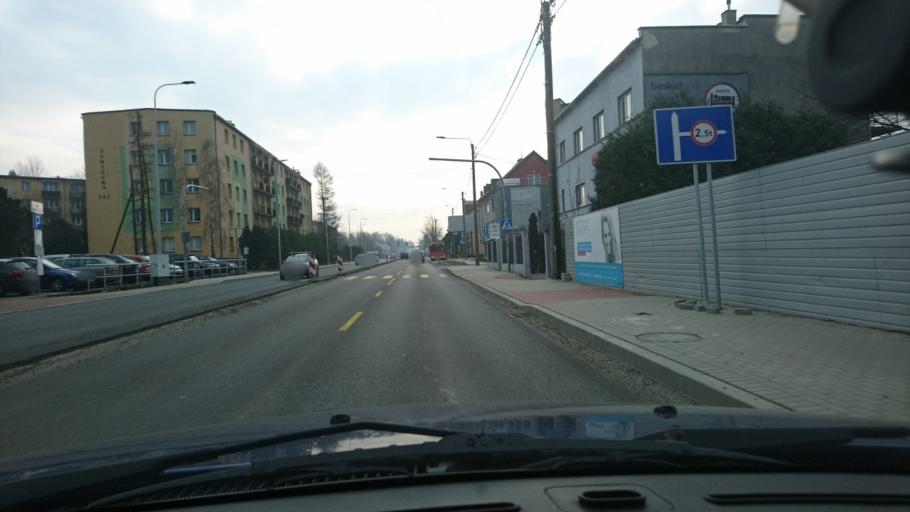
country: PL
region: Silesian Voivodeship
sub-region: Bielsko-Biala
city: Bielsko-Biala
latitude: 49.8031
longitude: 19.0580
